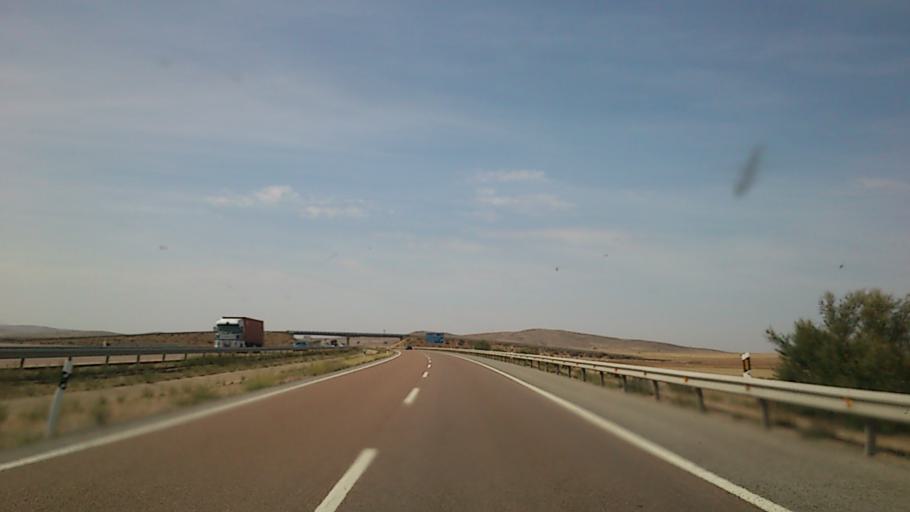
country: ES
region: Aragon
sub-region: Provincia de Teruel
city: Singra
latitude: 40.6114
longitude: -1.2877
